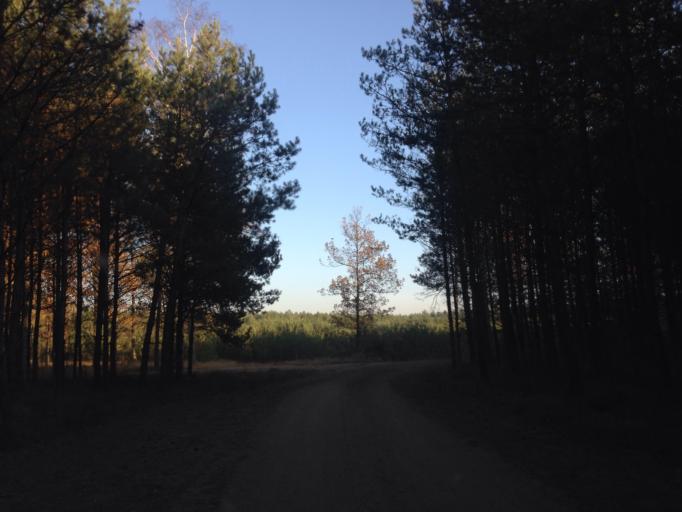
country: PL
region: Kujawsko-Pomorskie
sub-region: Powiat brodnicki
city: Gorzno
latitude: 53.1571
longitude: 19.6997
